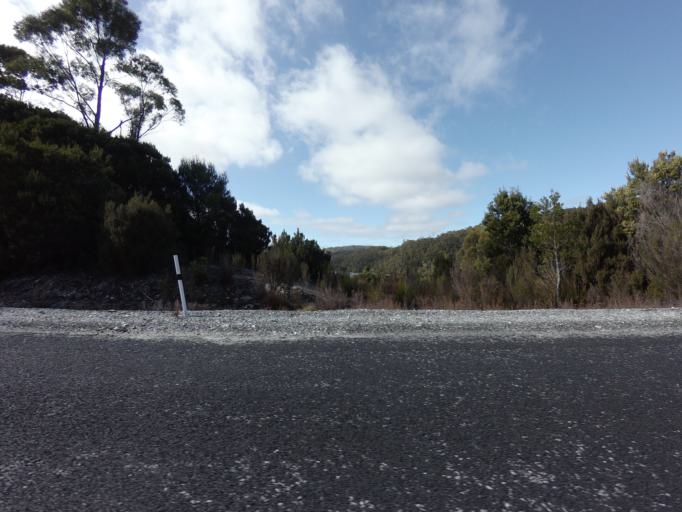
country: AU
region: Tasmania
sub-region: West Coast
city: Queenstown
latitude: -42.7958
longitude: 146.0825
